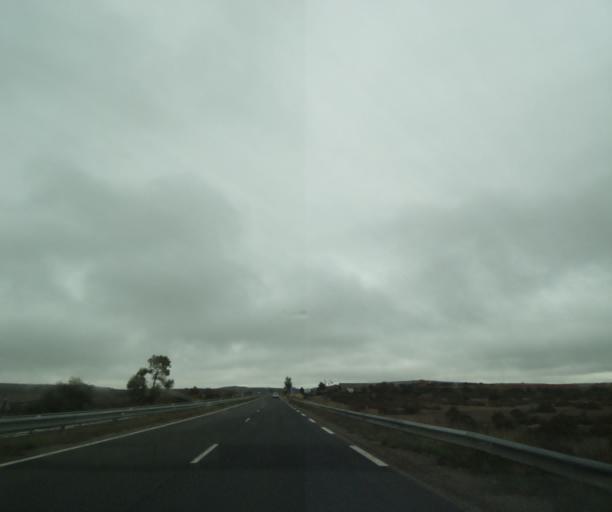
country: FR
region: Midi-Pyrenees
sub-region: Departement de l'Aveyron
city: Millau
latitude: 44.0719
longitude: 3.1133
